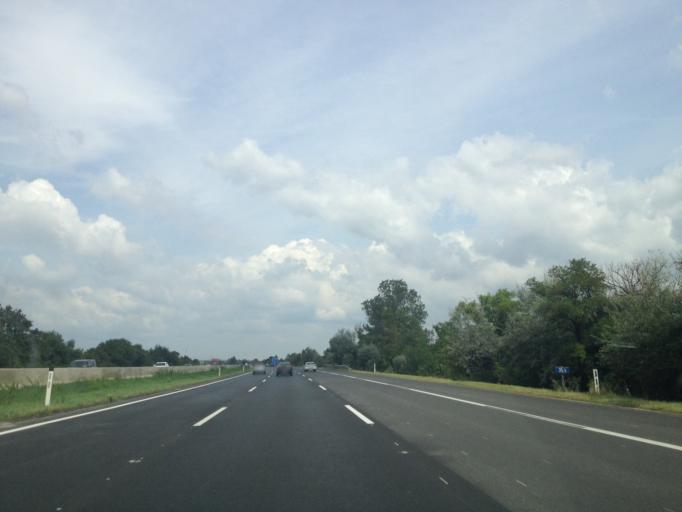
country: AT
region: Lower Austria
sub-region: Politischer Bezirk Wiener Neustadt
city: Felixdorf
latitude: 47.8792
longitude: 16.2030
